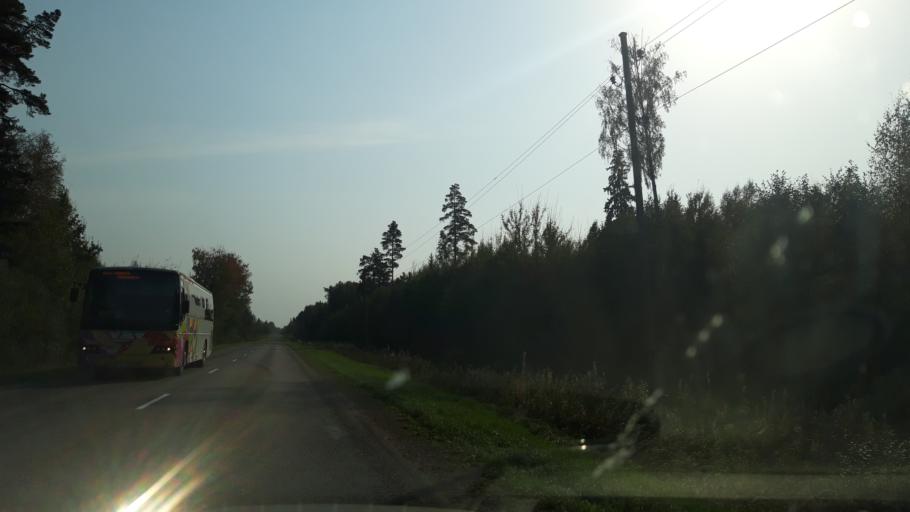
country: LV
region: Burtnieki
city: Matisi
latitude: 57.6449
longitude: 25.2440
